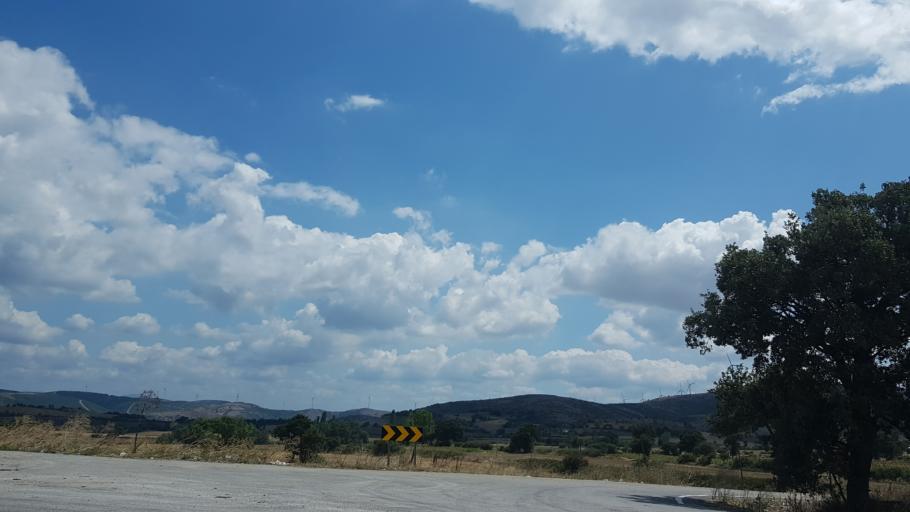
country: TR
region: Balikesir
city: Yenikoy
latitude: 39.7805
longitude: 28.0481
